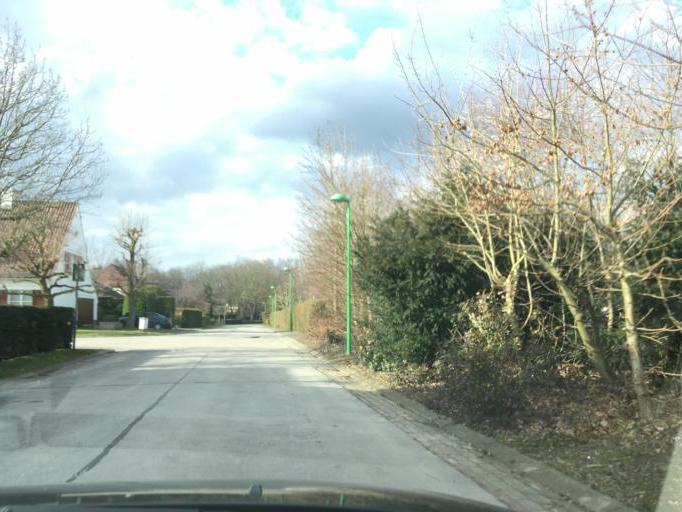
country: BE
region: Flanders
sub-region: Provincie West-Vlaanderen
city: Roeselare
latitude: 50.9253
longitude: 3.1453
